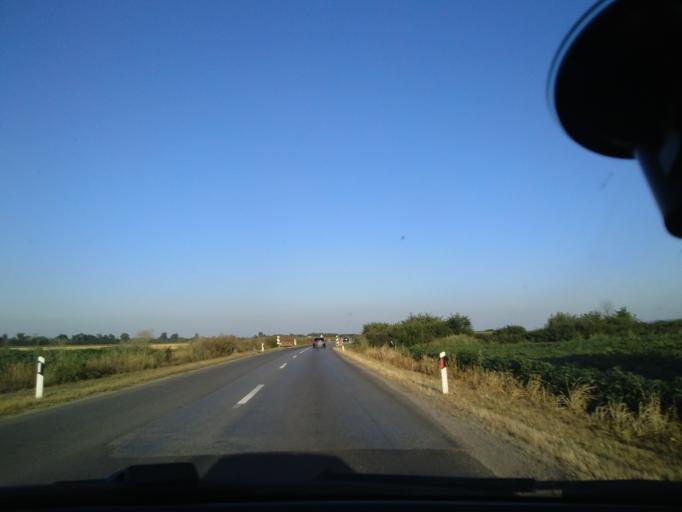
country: RS
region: Autonomna Pokrajina Vojvodina
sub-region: Juznobacki Okrug
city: Backi Petrovac
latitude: 45.3424
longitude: 19.6450
